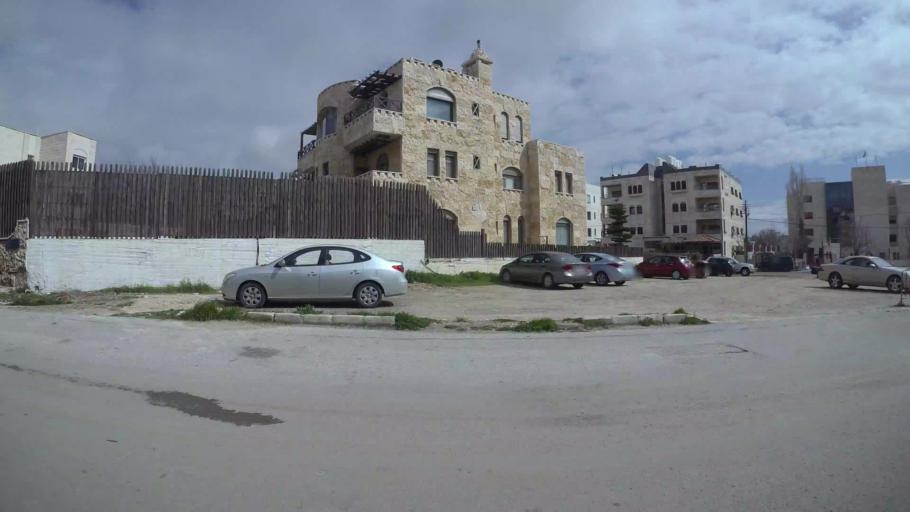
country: JO
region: Amman
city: Al Jubayhah
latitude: 31.9995
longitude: 35.8350
